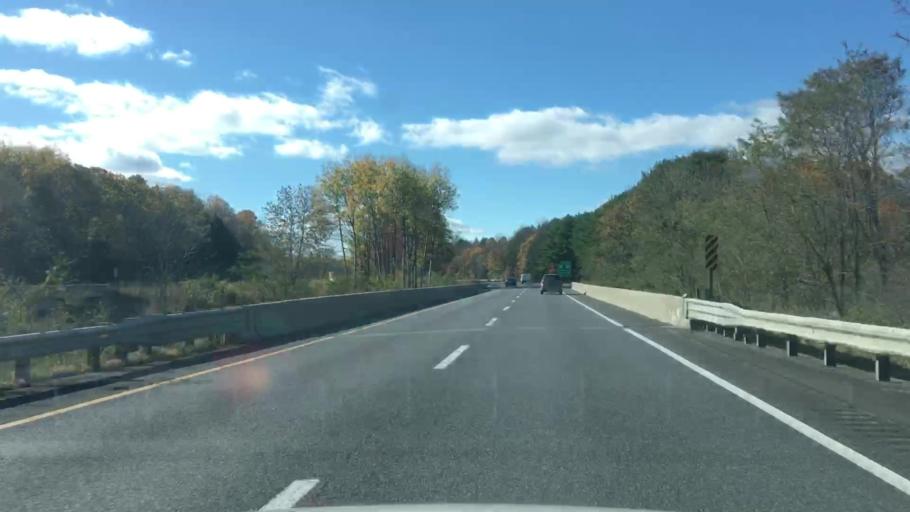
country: US
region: Maine
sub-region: Kennebec County
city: Waterville
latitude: 44.5718
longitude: -69.6557
